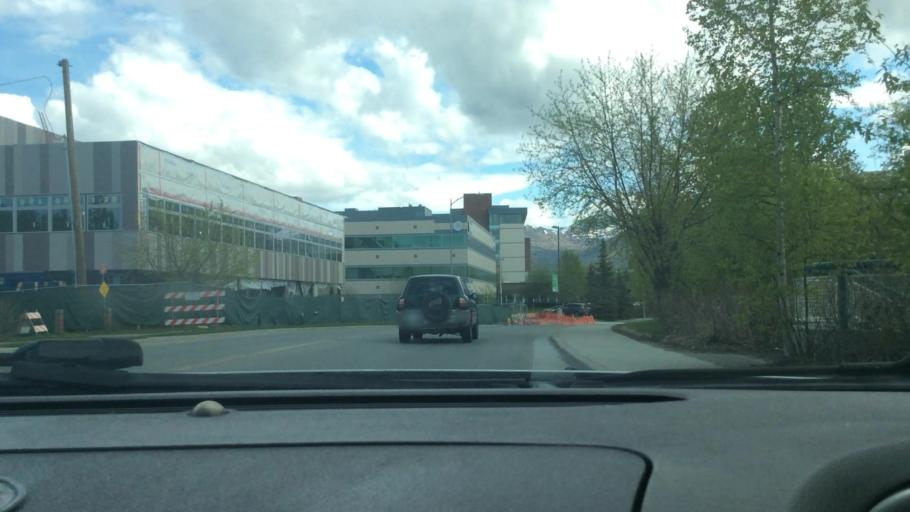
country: US
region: Alaska
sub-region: Anchorage Municipality
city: Anchorage
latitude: 61.1836
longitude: -149.8053
